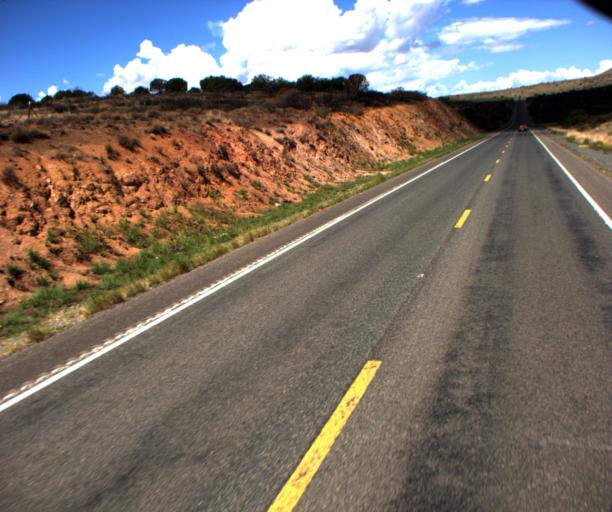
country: US
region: Arizona
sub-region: Yavapai County
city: Camp Verde
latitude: 34.5182
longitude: -112.0298
